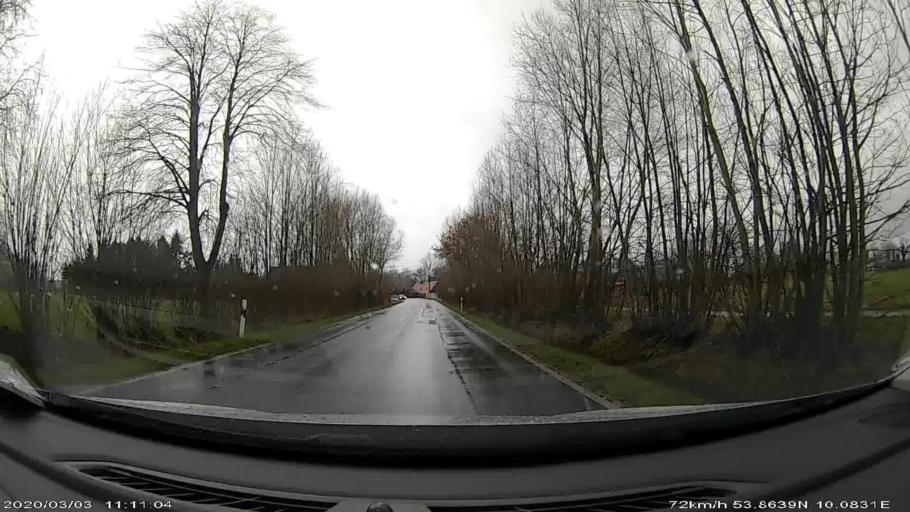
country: DE
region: Schleswig-Holstein
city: Sievershutten
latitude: 53.8648
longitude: 10.0801
